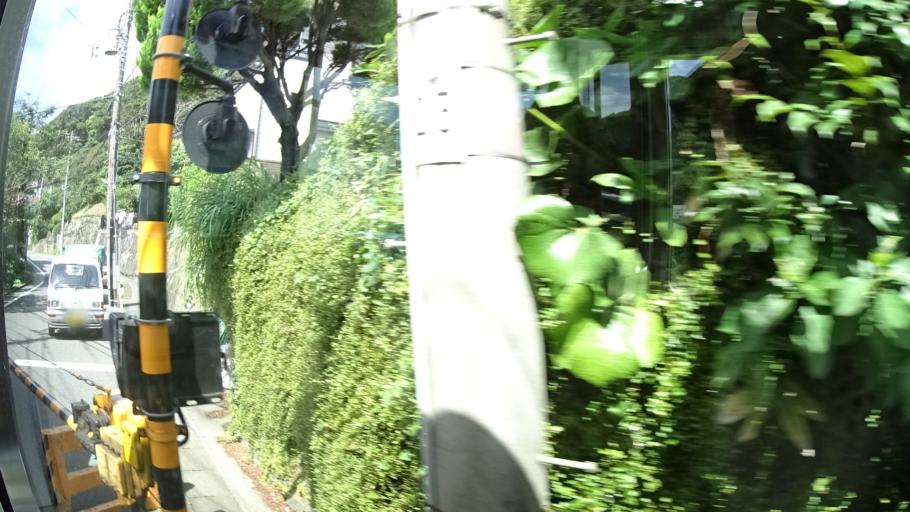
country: JP
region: Kanagawa
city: Kamakura
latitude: 35.3056
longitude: 139.5252
